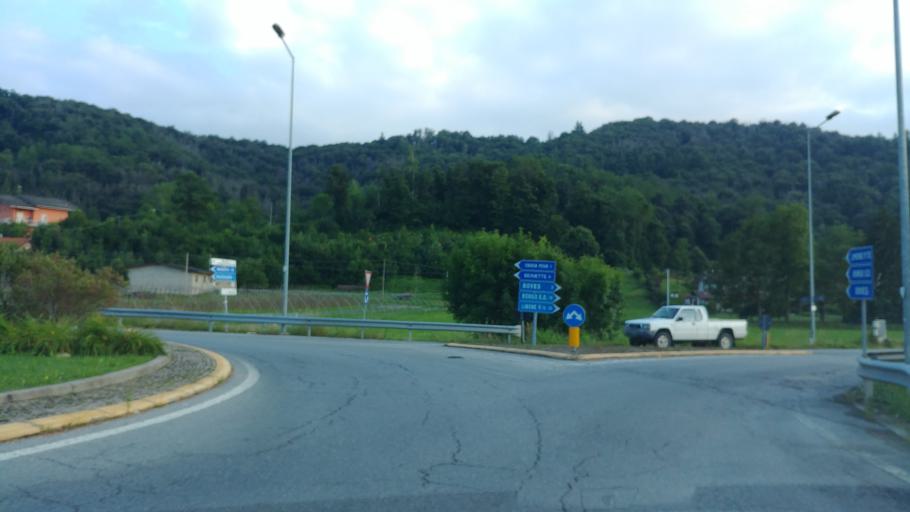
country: IT
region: Piedmont
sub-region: Provincia di Cuneo
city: Peveragno
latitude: 44.3354
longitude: 7.6055
